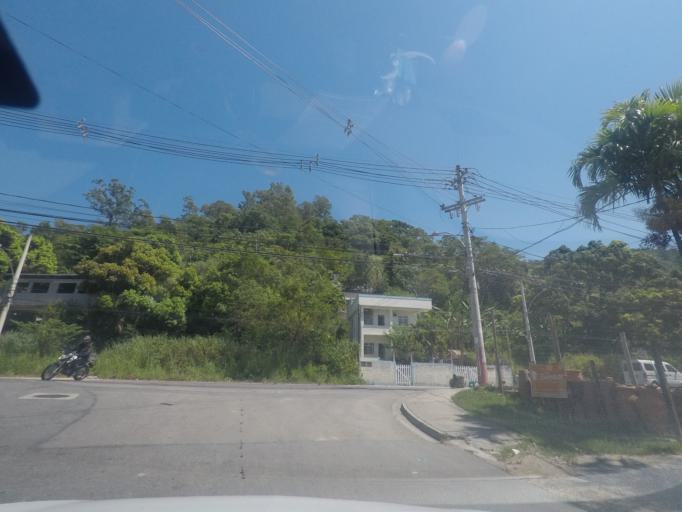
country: BR
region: Rio de Janeiro
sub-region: Nilopolis
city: Nilopolis
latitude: -22.9880
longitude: -43.4854
